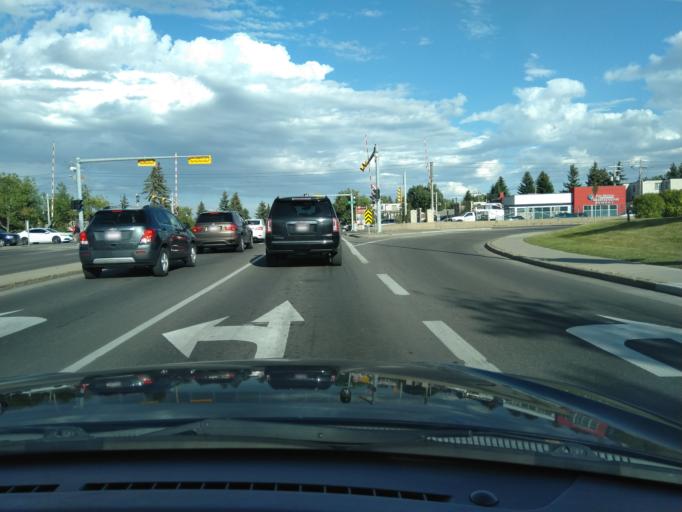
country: CA
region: Alberta
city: Calgary
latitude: 51.0778
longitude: -113.9826
